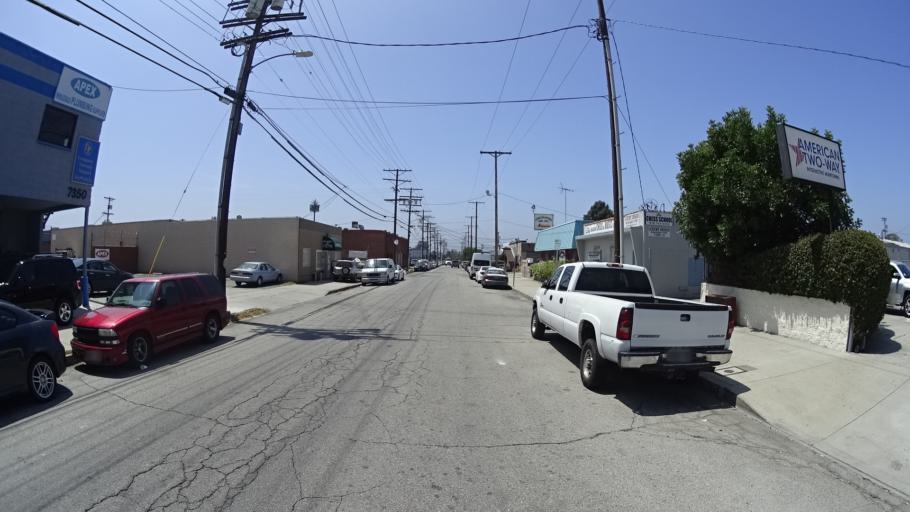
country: US
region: California
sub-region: Los Angeles County
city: Van Nuys
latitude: 34.2045
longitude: -118.4248
